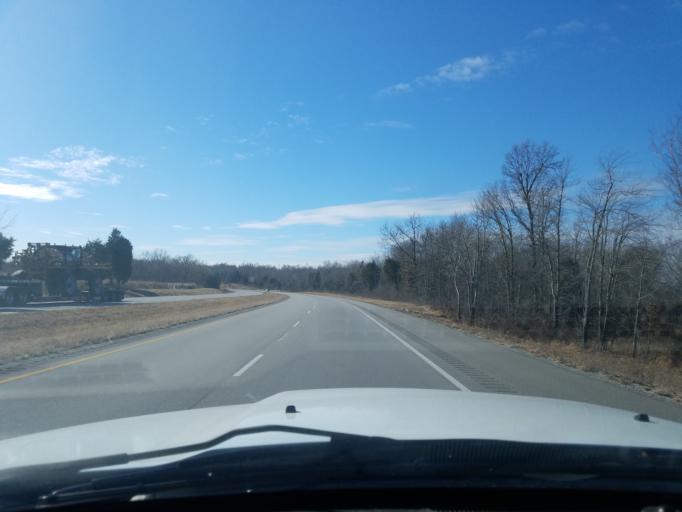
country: US
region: Kentucky
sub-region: Grayson County
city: Leitchfield
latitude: 37.5500
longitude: -86.1181
